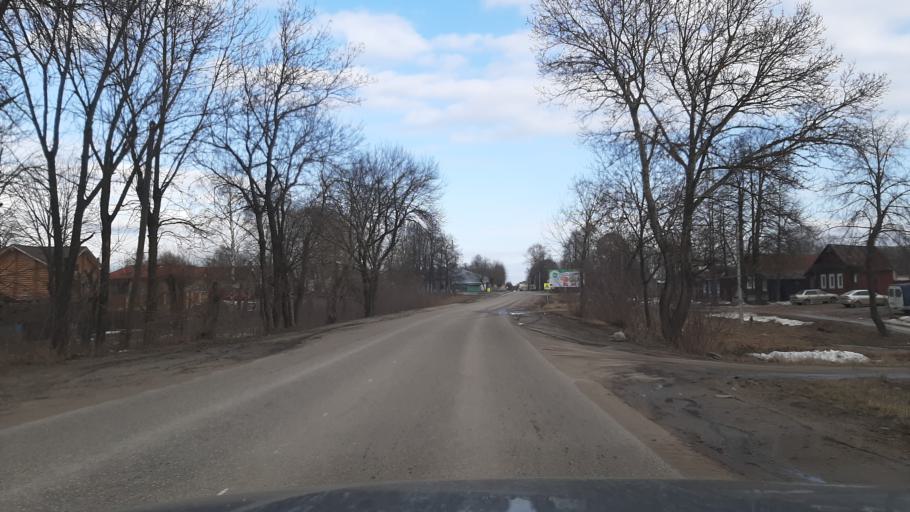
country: RU
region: Ivanovo
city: Teykovo
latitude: 56.8549
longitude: 40.5234
